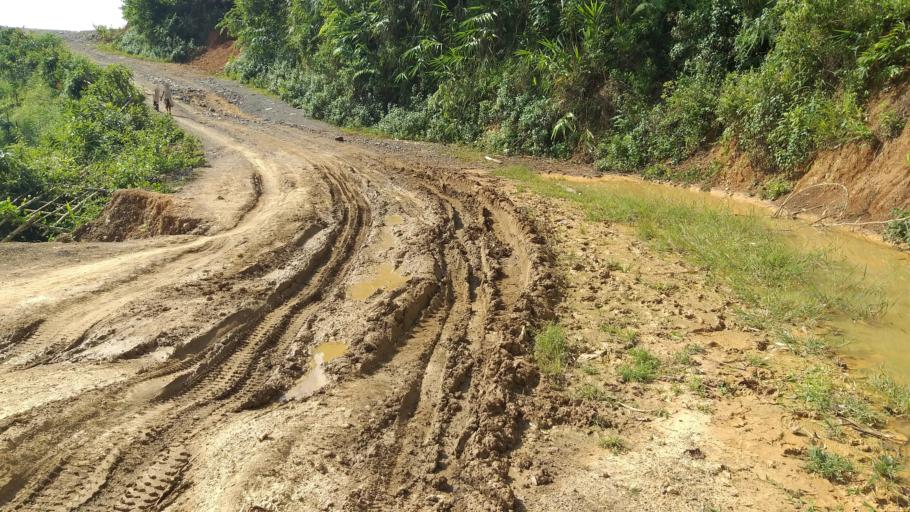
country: LA
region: Phongsali
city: Khoa
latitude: 21.2228
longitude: 102.5976
